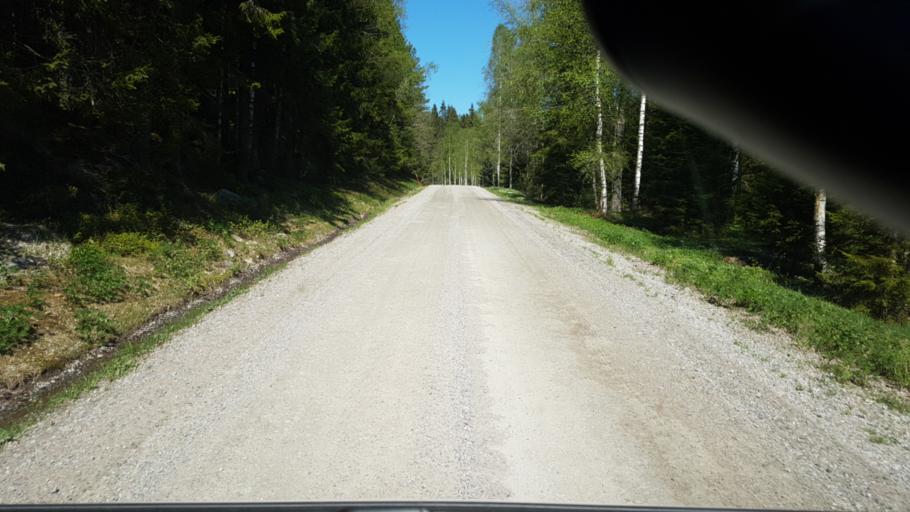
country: SE
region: Vaermland
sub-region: Arvika Kommun
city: Arvika
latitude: 59.8149
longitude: 12.7455
